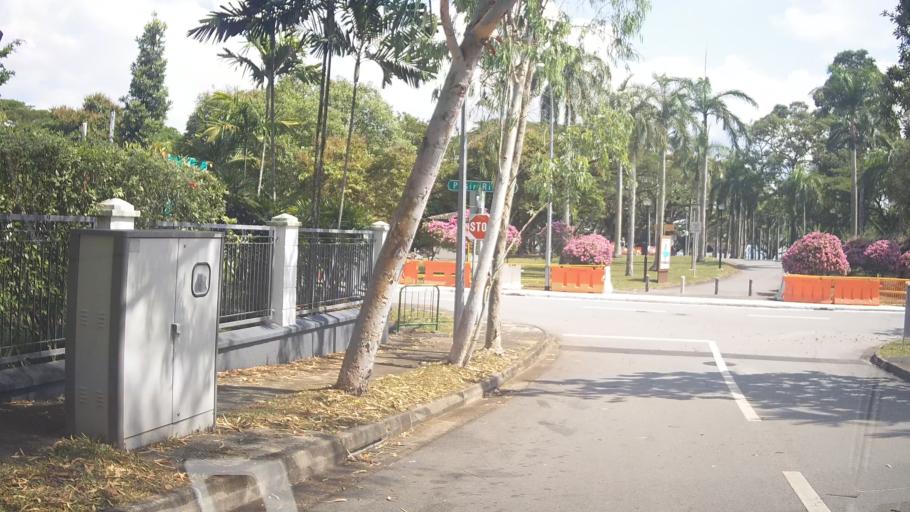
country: MY
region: Johor
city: Kampung Pasir Gudang Baru
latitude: 1.3826
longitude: 103.9453
